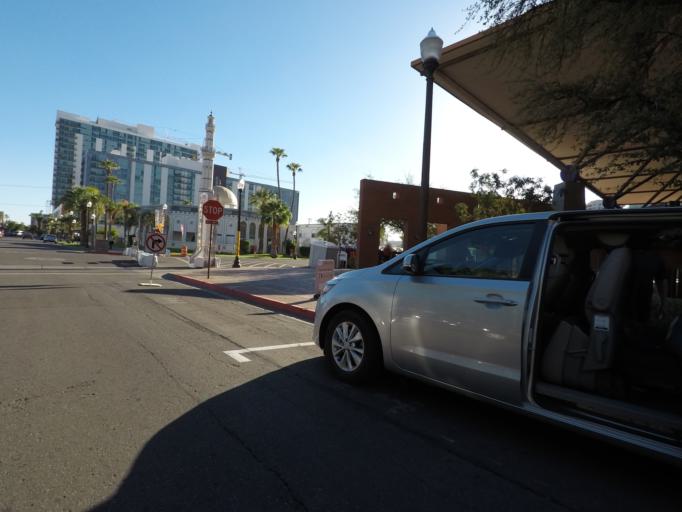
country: US
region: Arizona
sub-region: Maricopa County
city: Tempe Junction
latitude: 33.4246
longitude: -111.9367
